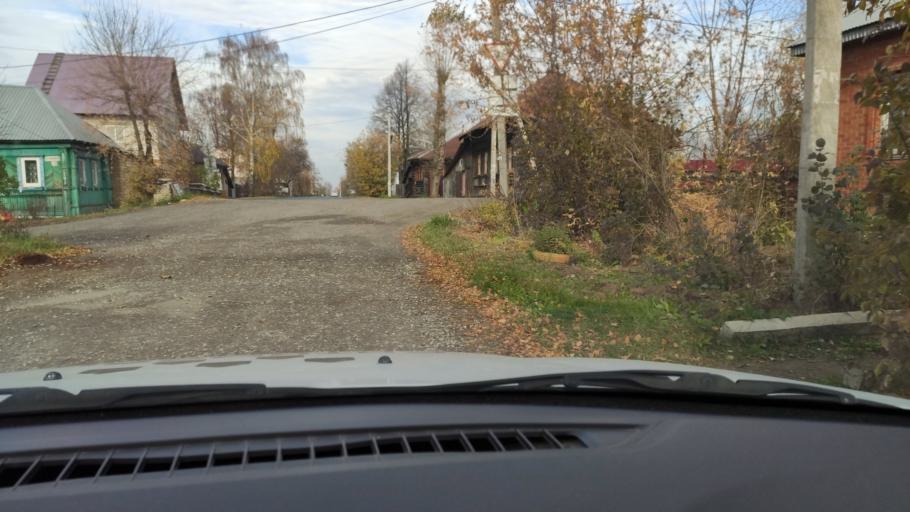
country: RU
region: Perm
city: Perm
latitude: 58.0344
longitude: 56.3410
